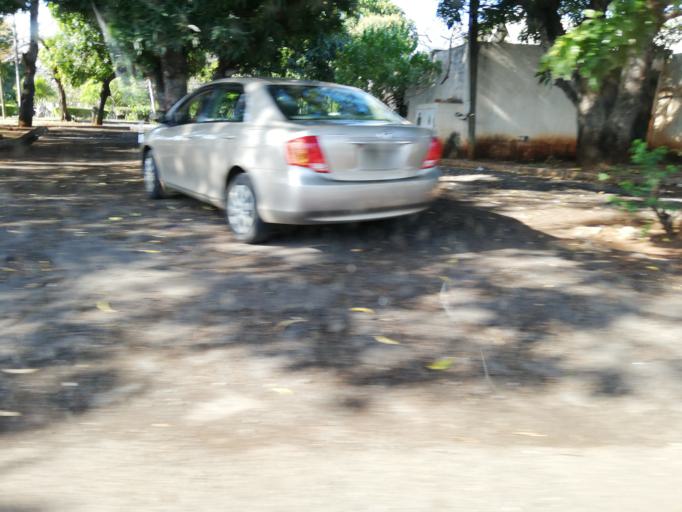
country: MU
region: Port Louis
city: Port Louis
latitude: -20.1594
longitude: 57.4872
